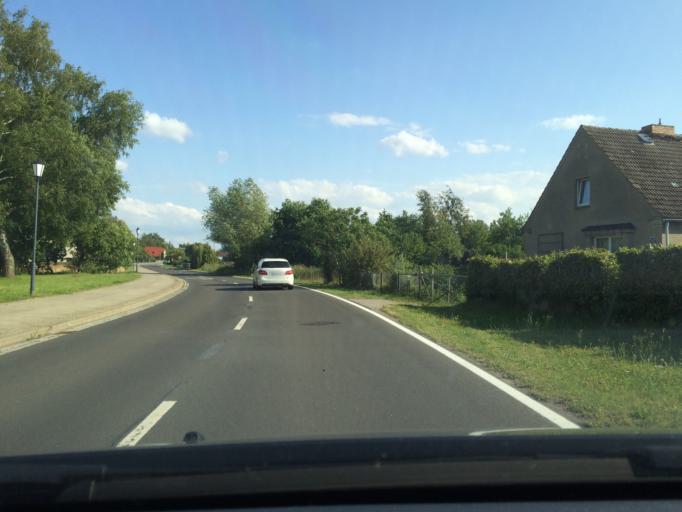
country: DE
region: Mecklenburg-Vorpommern
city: Niepars
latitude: 54.3116
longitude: 12.9227
